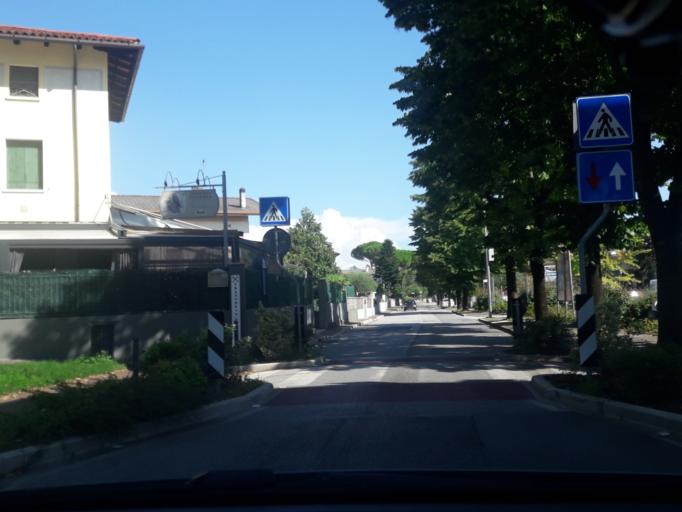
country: IT
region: Friuli Venezia Giulia
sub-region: Provincia di Udine
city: Feletto Umberto
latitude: 46.1009
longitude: 13.2165
